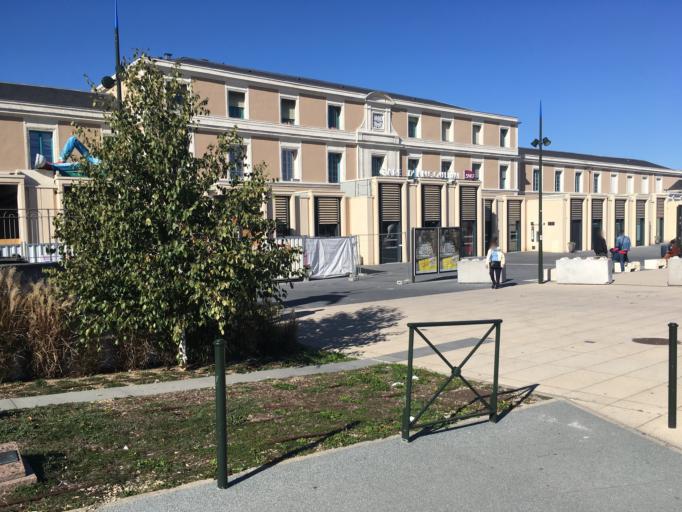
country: FR
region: Poitou-Charentes
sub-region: Departement de la Charente
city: Angouleme
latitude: 45.6532
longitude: 0.1647
